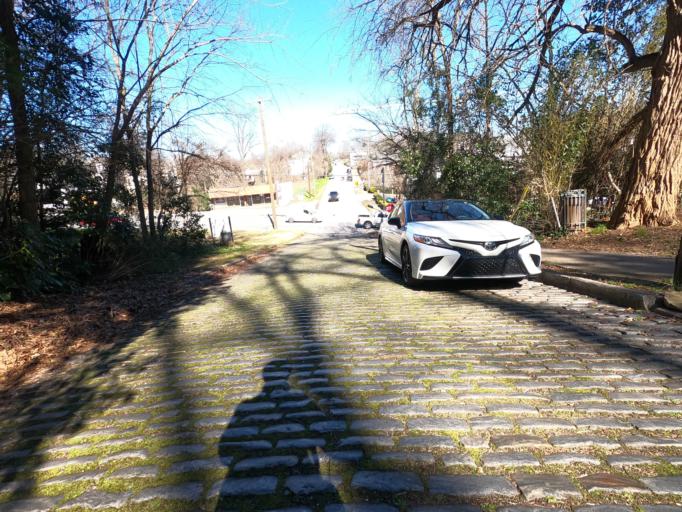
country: US
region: Georgia
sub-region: Clarke County
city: Athens
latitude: 33.9559
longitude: -83.3826
